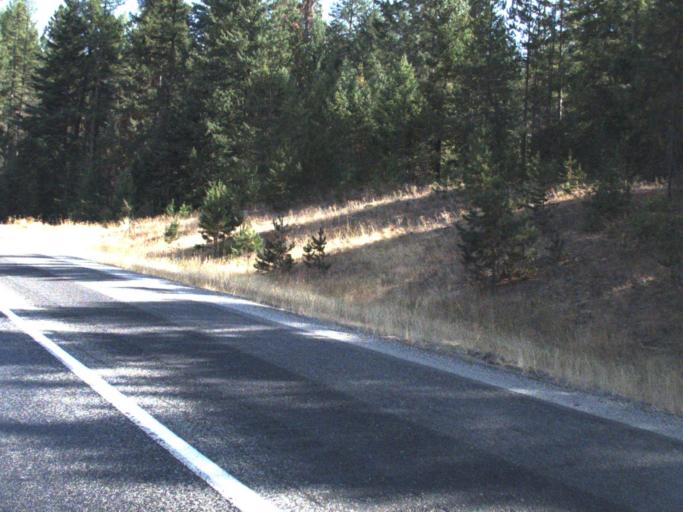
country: US
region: Washington
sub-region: Spokane County
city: Deer Park
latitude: 48.0967
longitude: -117.2904
